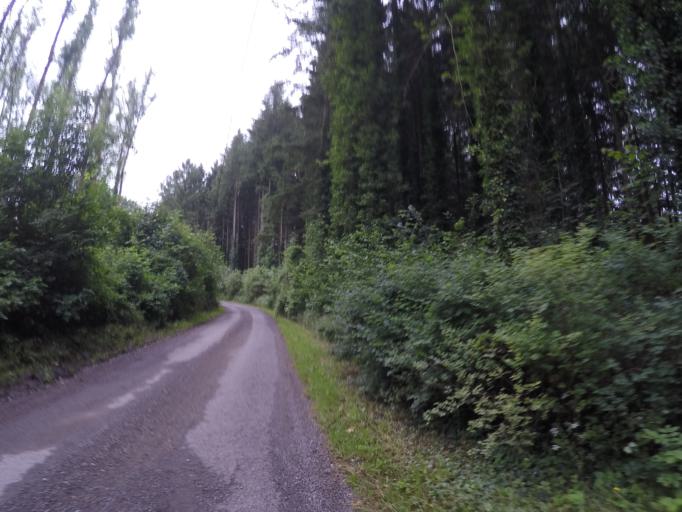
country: BE
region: Wallonia
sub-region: Province de Namur
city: Yvoir
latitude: 50.3287
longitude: 4.9247
